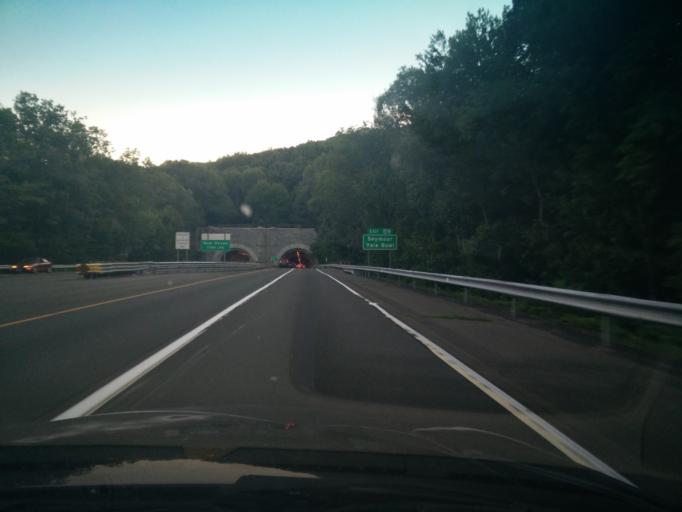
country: US
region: Connecticut
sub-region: New Haven County
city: Woodbridge
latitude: 41.3478
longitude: -72.9674
